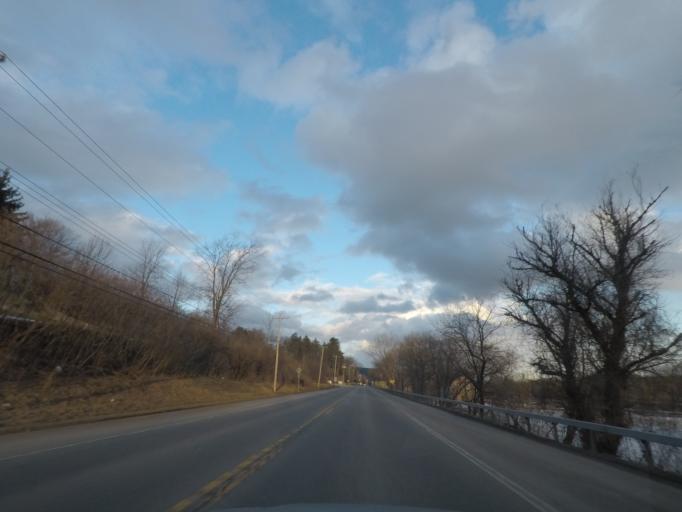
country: US
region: New York
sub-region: Montgomery County
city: Saint Johnsville
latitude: 42.9984
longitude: -74.6965
